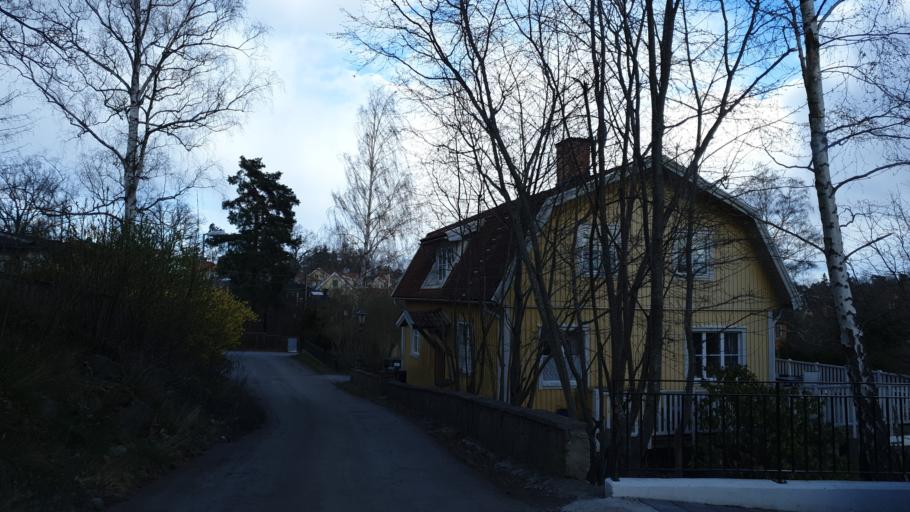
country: SE
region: Stockholm
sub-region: Lidingo
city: Lidingoe
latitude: 59.3709
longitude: 18.1202
